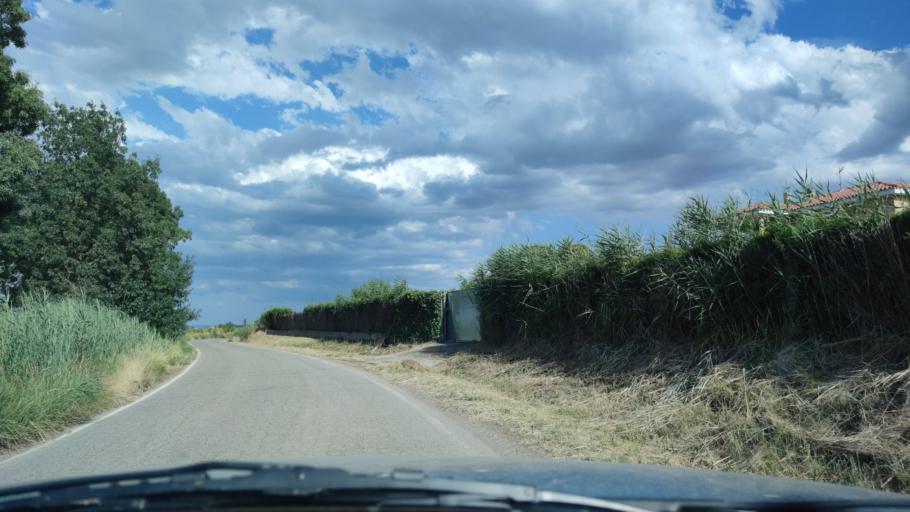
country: ES
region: Catalonia
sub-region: Provincia de Lleida
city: Alpicat
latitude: 41.6276
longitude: 0.5734
